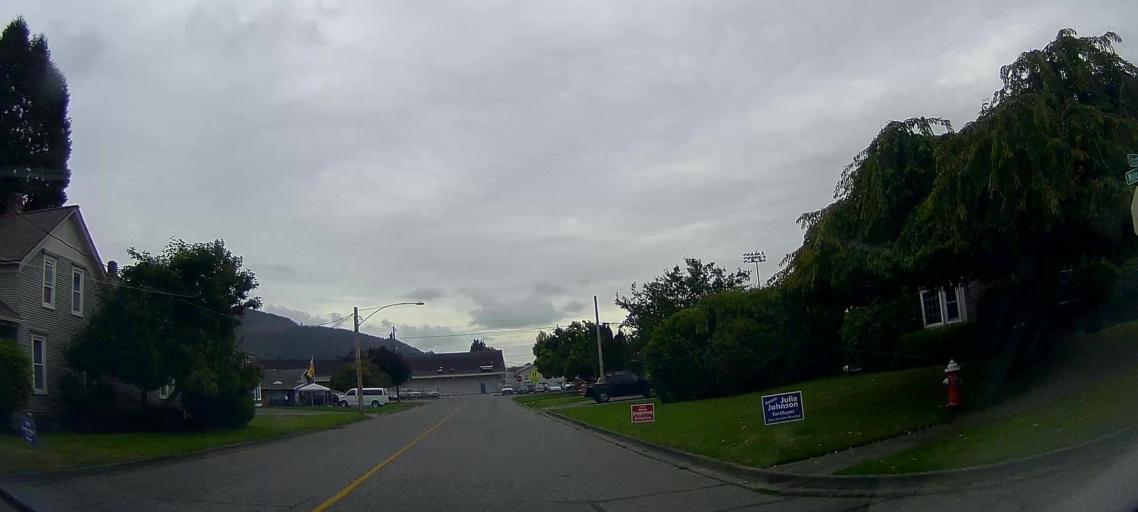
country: US
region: Washington
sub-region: Skagit County
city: Sedro-Woolley
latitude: 48.5015
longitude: -122.2387
